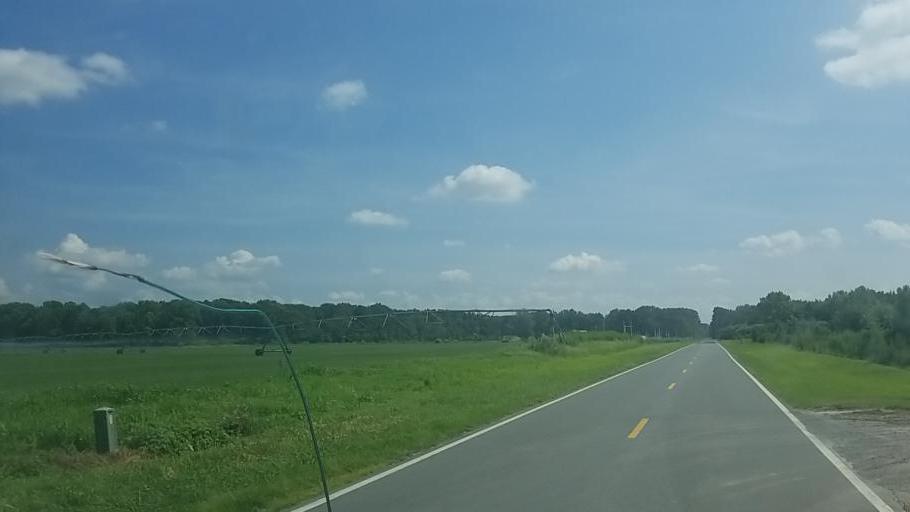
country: US
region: Maryland
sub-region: Wicomico County
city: Hebron
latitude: 38.4293
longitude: -75.6978
